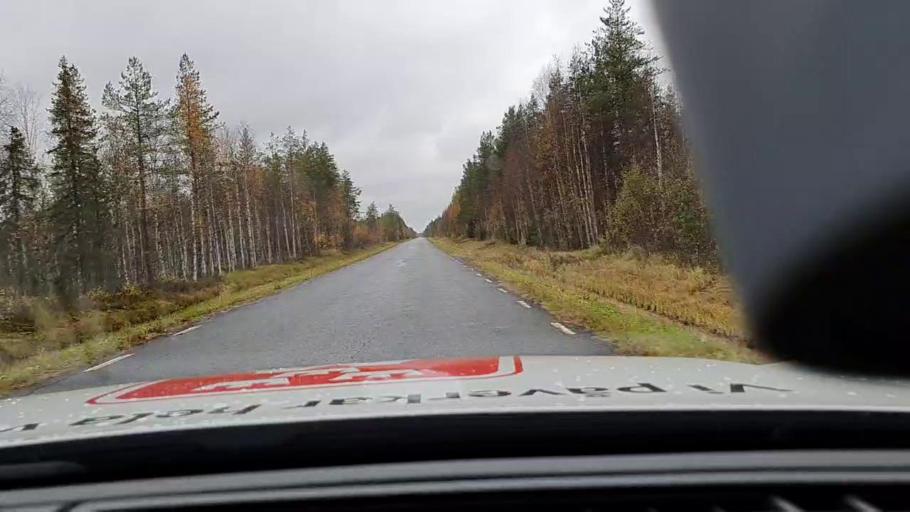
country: SE
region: Norrbotten
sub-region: Haparanda Kommun
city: Haparanda
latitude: 65.9060
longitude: 23.8325
